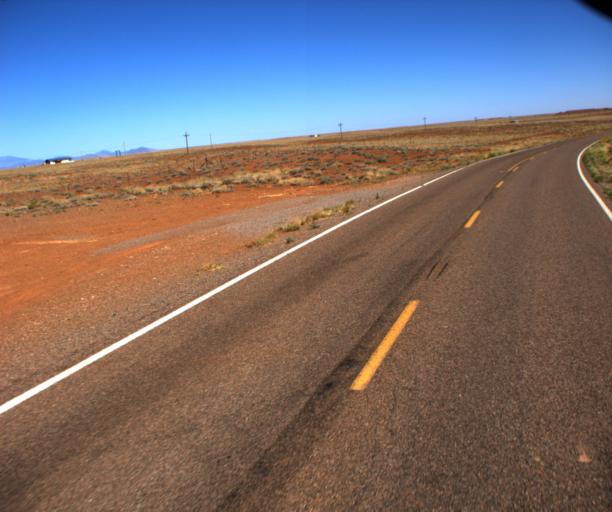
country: US
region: Arizona
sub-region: Coconino County
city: LeChee
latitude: 35.2017
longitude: -110.9466
